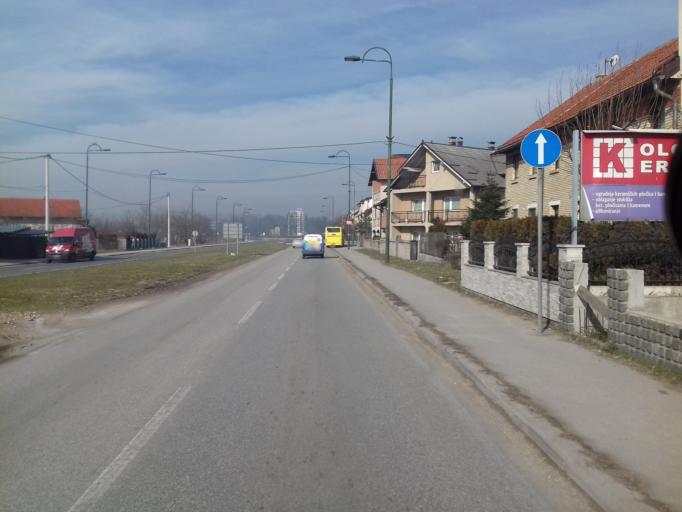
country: BA
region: Federation of Bosnia and Herzegovina
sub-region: Kanton Sarajevo
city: Sarajevo
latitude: 43.8166
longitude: 18.3086
